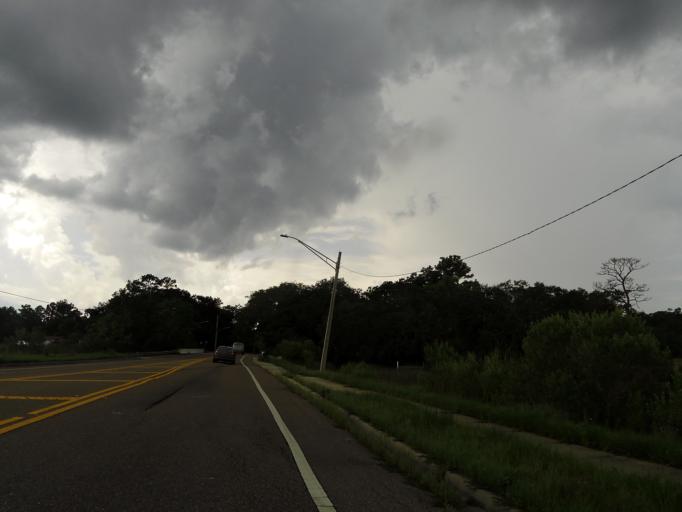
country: US
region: Florida
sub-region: Duval County
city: Jacksonville
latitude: 30.4221
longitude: -81.6883
